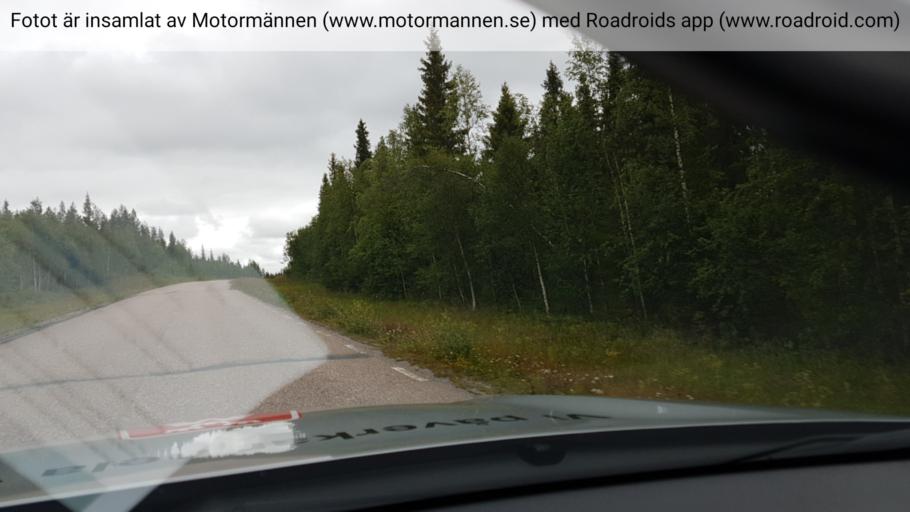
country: SE
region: Norrbotten
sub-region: Overkalix Kommun
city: OEverkalix
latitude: 67.0415
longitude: 22.0423
